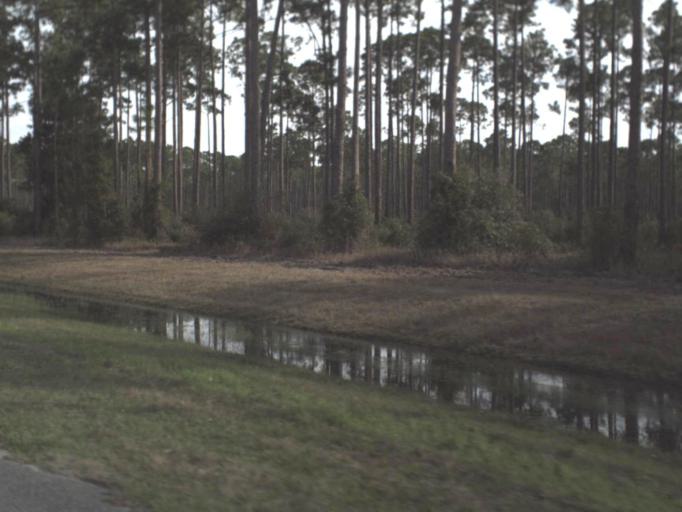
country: US
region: Florida
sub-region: Bay County
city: Mexico Beach
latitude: 29.9780
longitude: -85.4698
